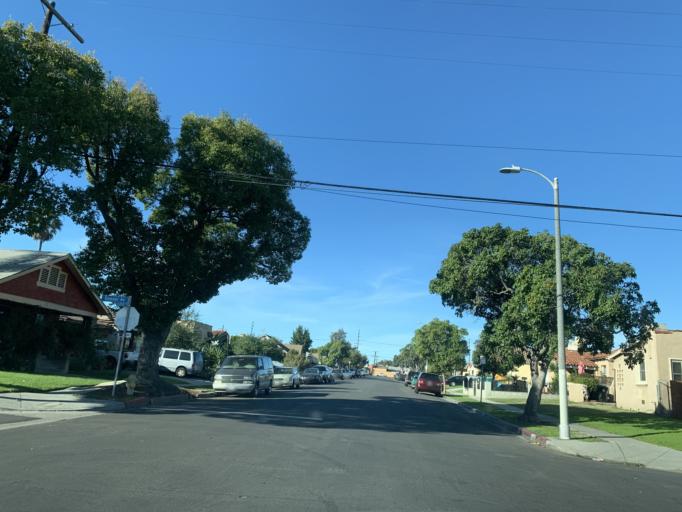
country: US
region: California
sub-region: Los Angeles County
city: Westmont
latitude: 33.9329
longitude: -118.2847
